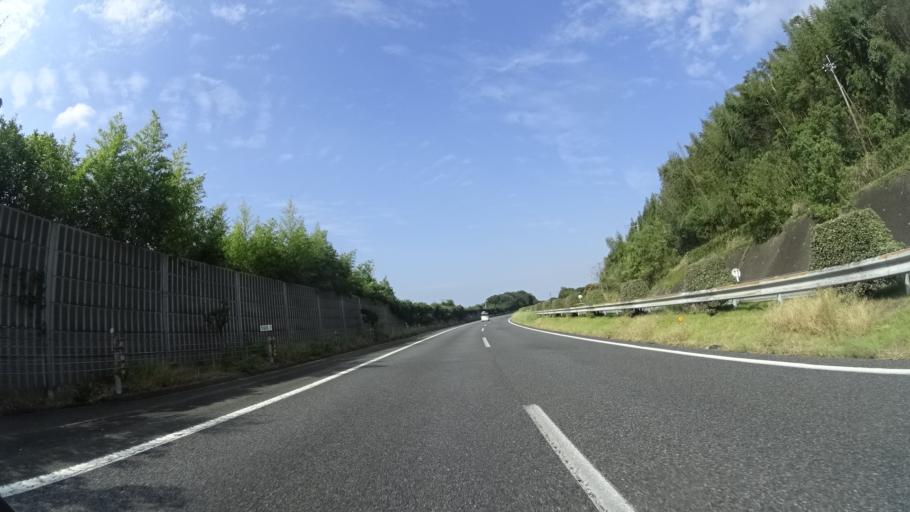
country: JP
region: Kumamoto
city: Matsubase
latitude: 32.6186
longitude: 130.7161
